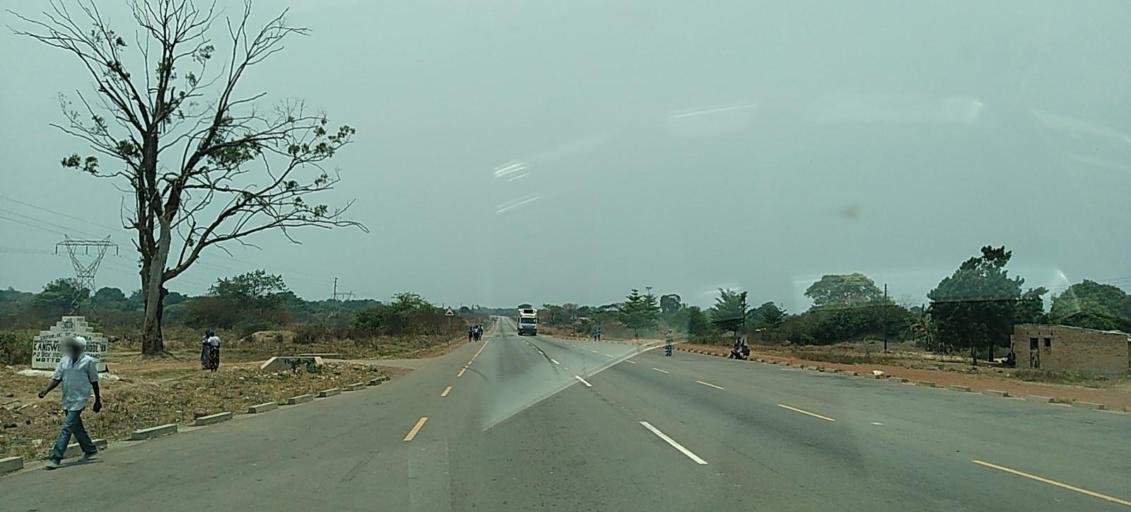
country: ZM
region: Copperbelt
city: Chililabombwe
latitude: -12.3813
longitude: 27.3223
